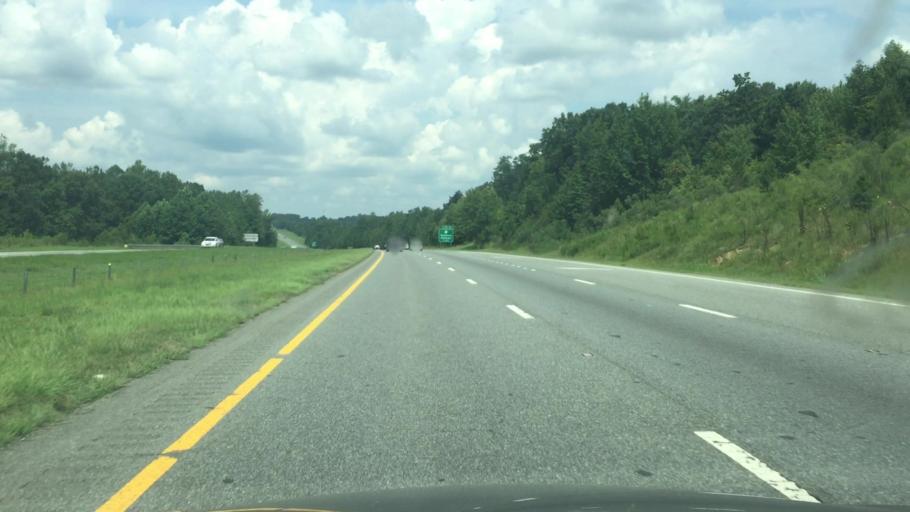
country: US
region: North Carolina
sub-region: Montgomery County
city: Biscoe
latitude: 35.5175
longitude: -79.7819
